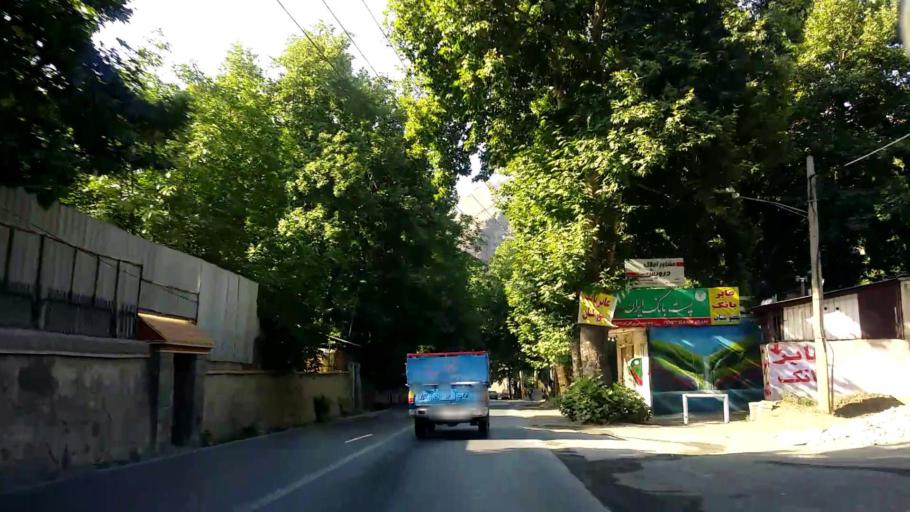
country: IR
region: Alborz
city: Karaj
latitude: 35.8829
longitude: 51.0416
